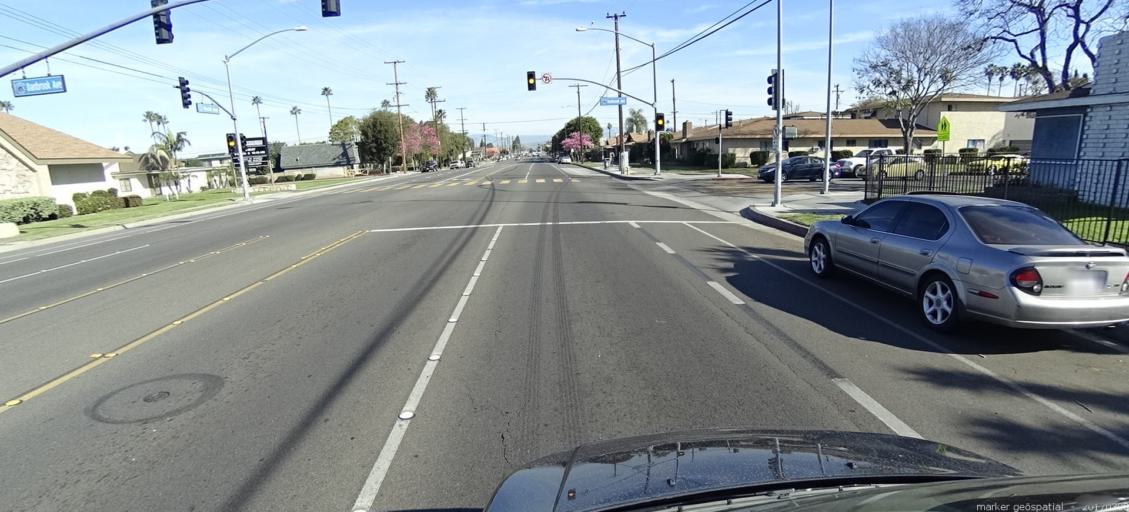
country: US
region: California
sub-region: Orange County
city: Cypress
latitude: 33.8275
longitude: -118.0109
